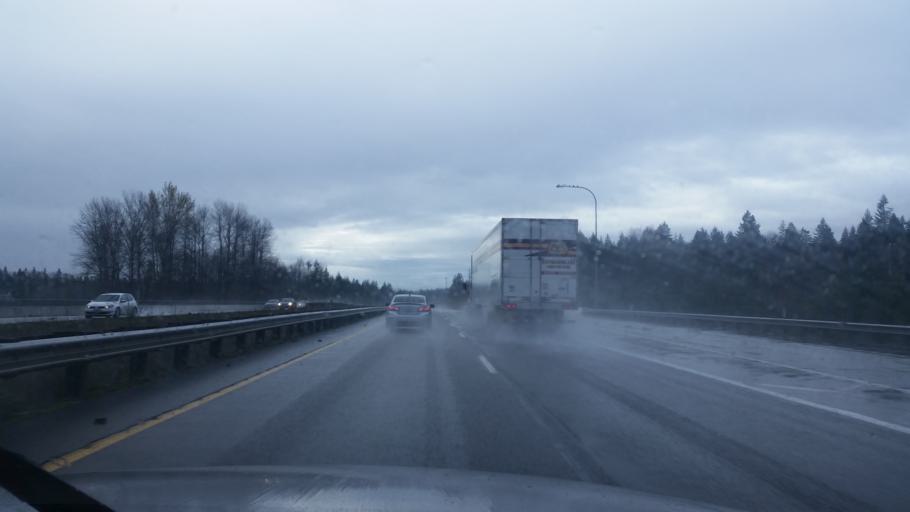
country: US
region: Washington
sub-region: King County
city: Maple Valley
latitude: 47.4165
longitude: -122.0143
